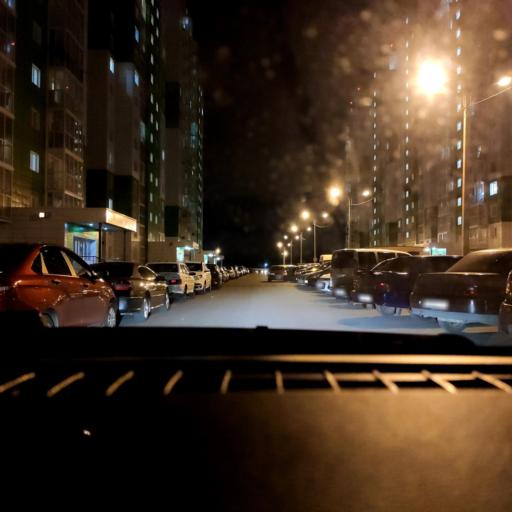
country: RU
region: Voronezj
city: Maslovka
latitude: 51.6349
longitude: 39.2962
